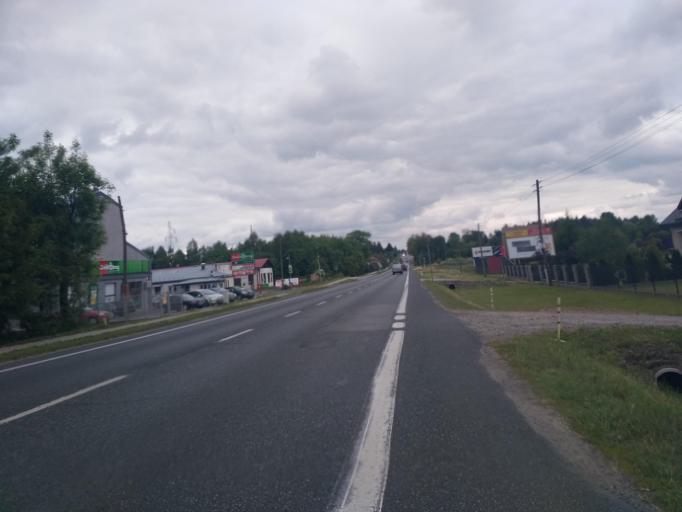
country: PL
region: Subcarpathian Voivodeship
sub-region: Powiat krosnienski
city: Jedlicze
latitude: 49.7223
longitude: 21.6961
